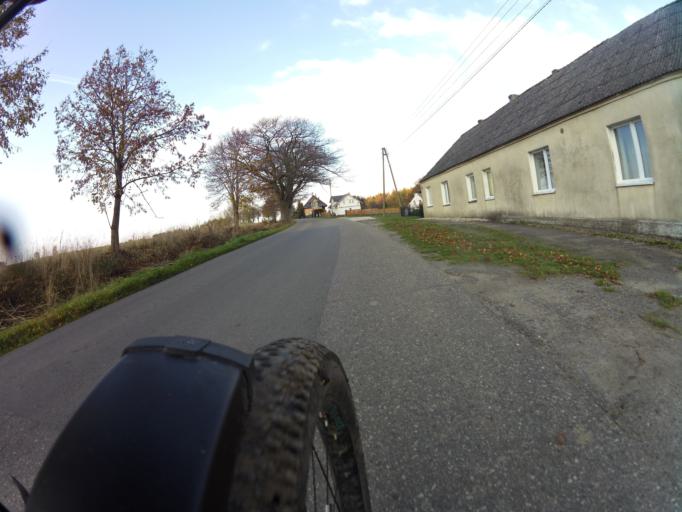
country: PL
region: Pomeranian Voivodeship
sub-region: Powiat pucki
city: Krokowa
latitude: 54.7539
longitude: 18.1845
